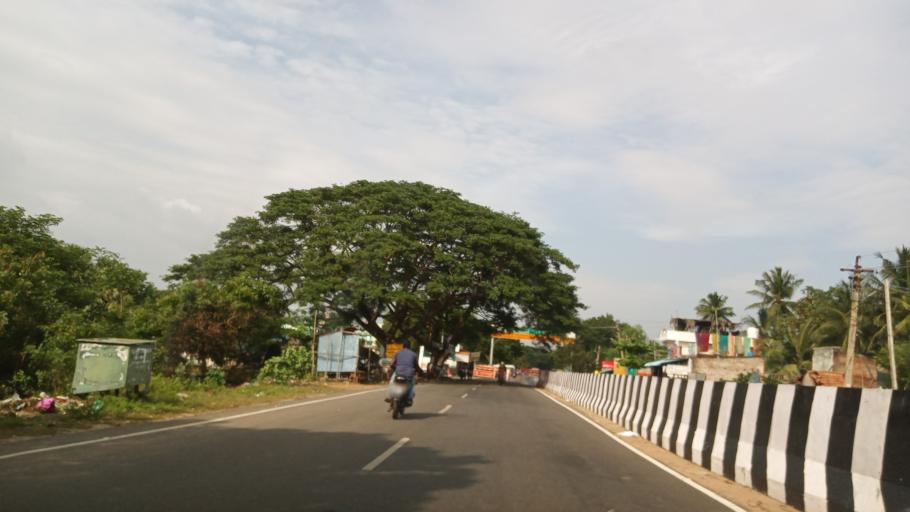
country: IN
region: Tamil Nadu
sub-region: Villupuram
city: Auroville
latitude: 12.0556
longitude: 79.8738
